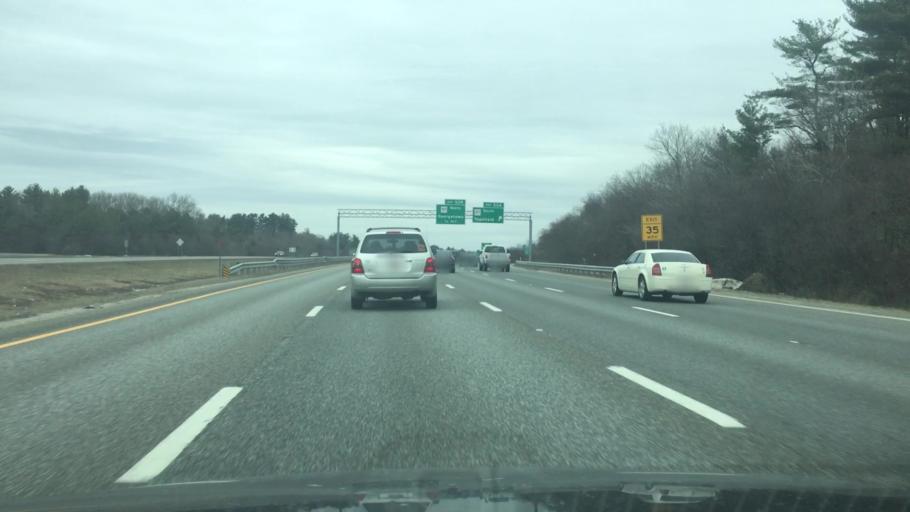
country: US
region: Massachusetts
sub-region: Essex County
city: Boxford
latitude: 42.6790
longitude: -70.9758
